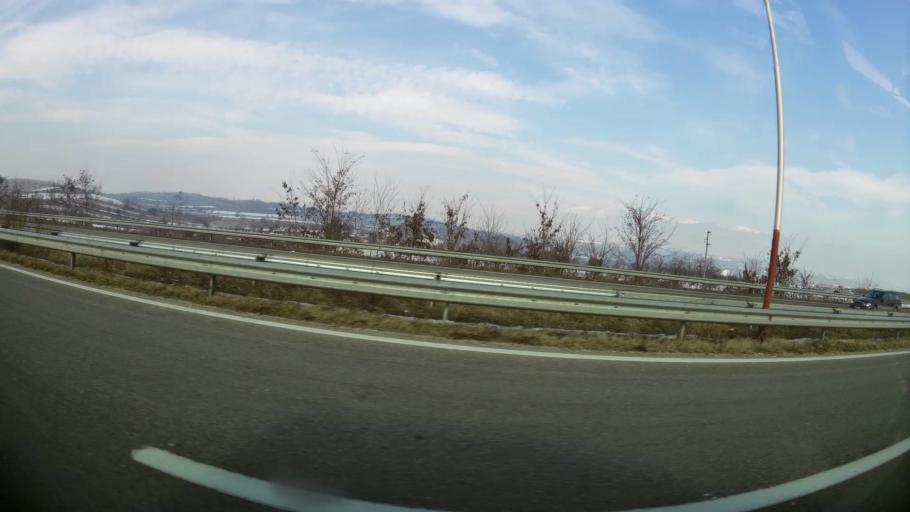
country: MK
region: Suto Orizari
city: Suto Orizare
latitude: 42.0518
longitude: 21.4261
